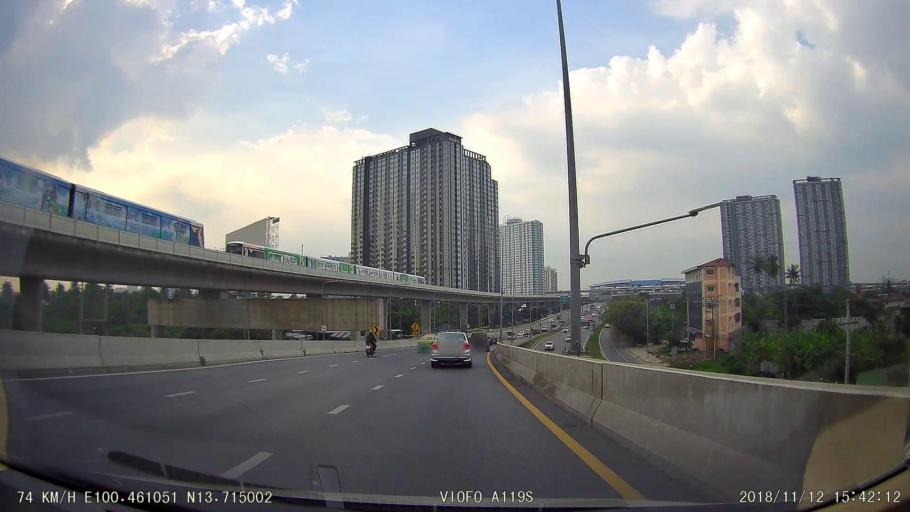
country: TH
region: Bangkok
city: Bangkok Yai
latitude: 13.7151
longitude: 100.4609
